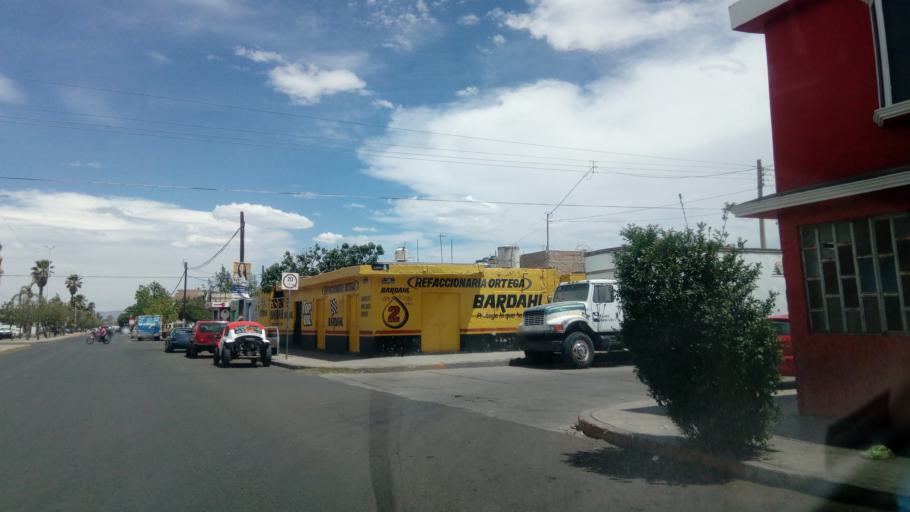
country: MX
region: Durango
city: Victoria de Durango
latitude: 23.9974
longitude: -104.6751
